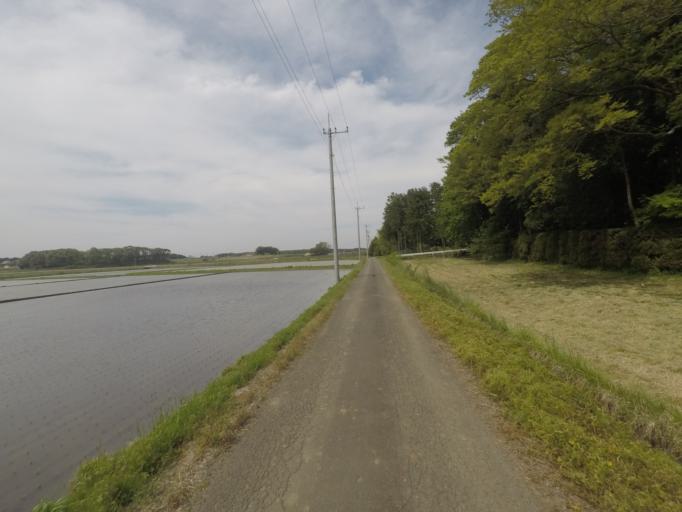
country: JP
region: Ibaraki
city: Tsukuba
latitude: 36.1836
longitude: 140.0382
